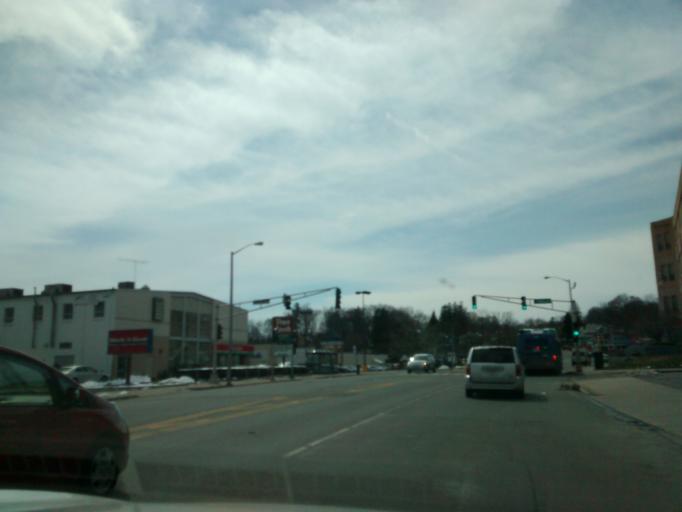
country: US
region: Massachusetts
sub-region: Worcester County
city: Worcester
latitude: 42.2430
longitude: -71.8417
